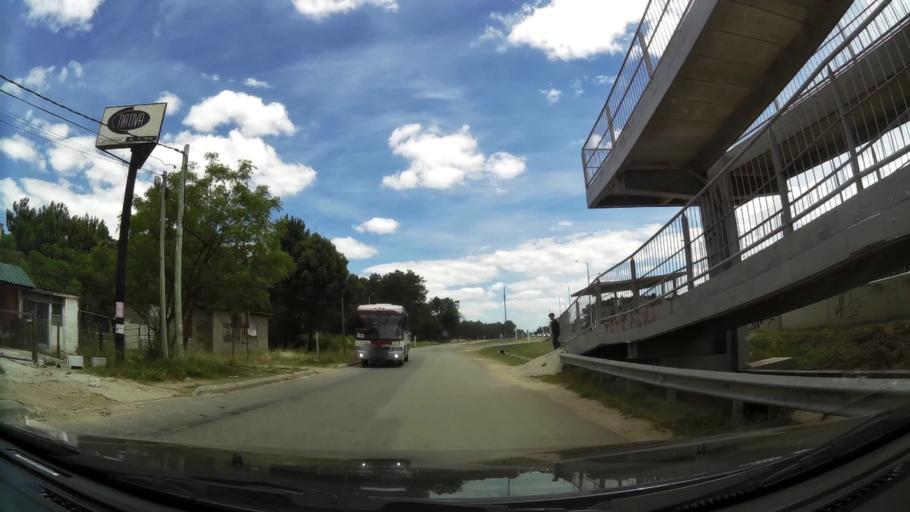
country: UY
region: Canelones
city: Empalme Olmos
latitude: -34.7880
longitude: -55.8928
